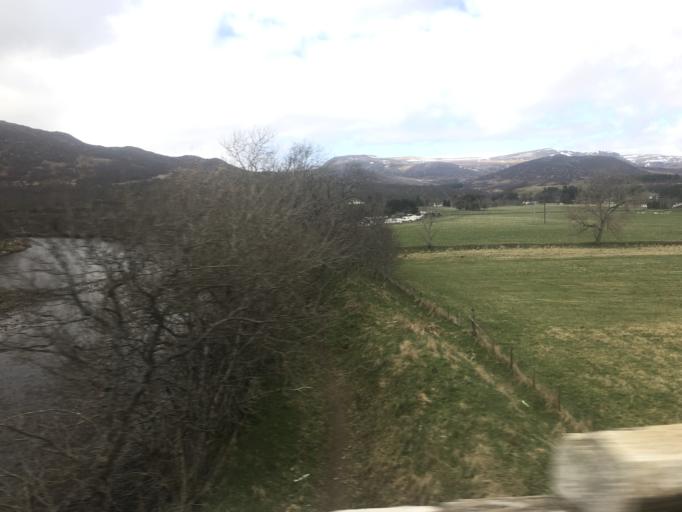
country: GB
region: Scotland
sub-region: Highland
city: Kingussie
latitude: 57.0546
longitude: -4.1256
